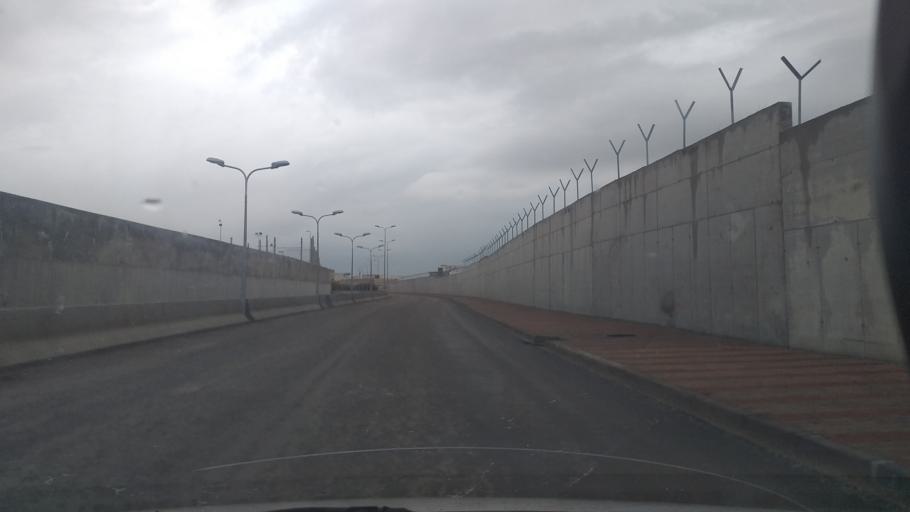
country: TN
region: Ariana
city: Ariana
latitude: 36.8567
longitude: 10.2134
